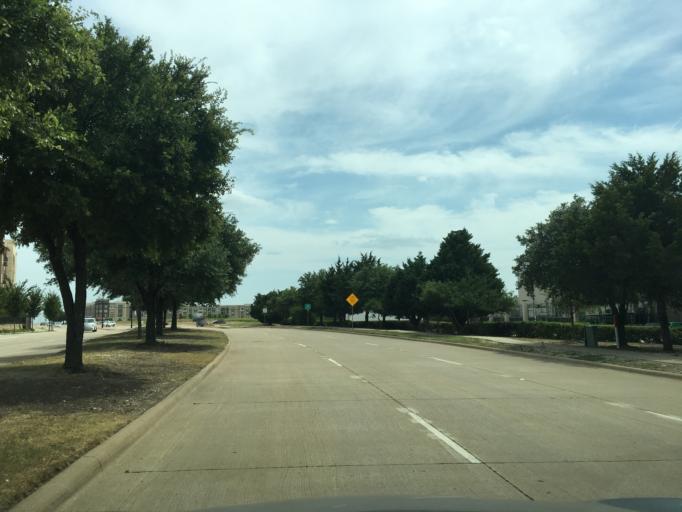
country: US
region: Texas
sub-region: Collin County
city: Frisco
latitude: 33.1070
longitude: -96.8013
